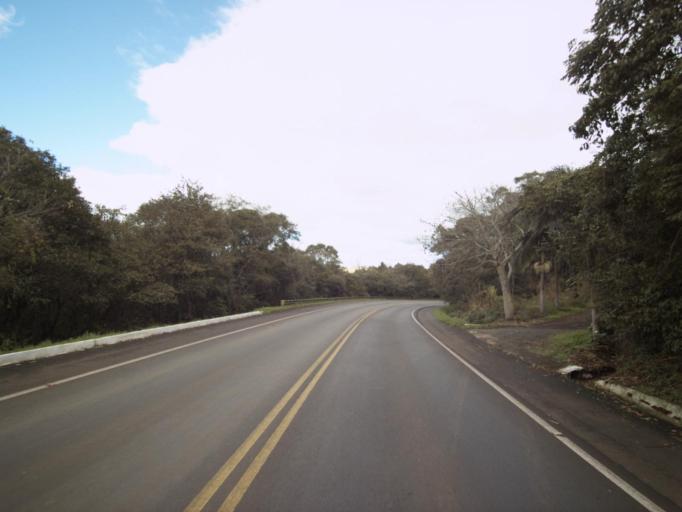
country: BR
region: Santa Catarina
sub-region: Concordia
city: Concordia
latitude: -27.3566
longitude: -51.9878
